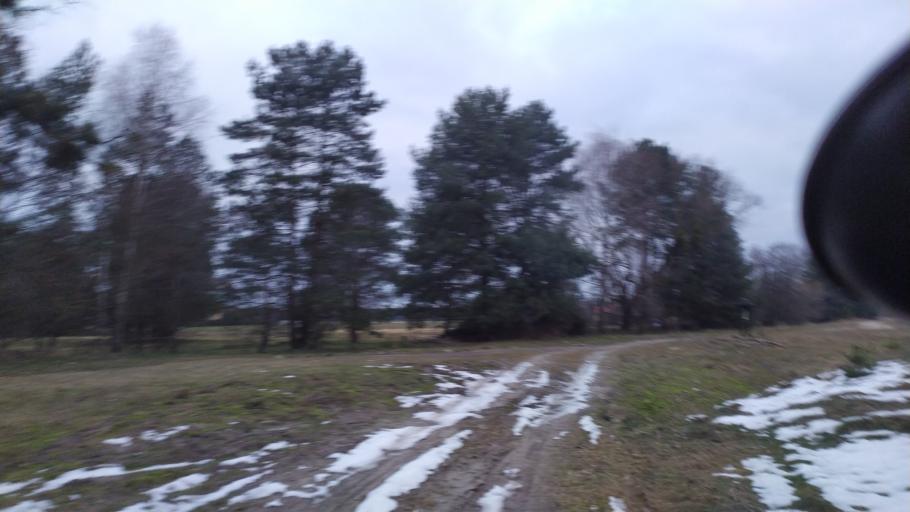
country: PL
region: Lublin Voivodeship
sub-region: Powiat lubartowski
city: Abramow
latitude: 51.4242
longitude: 22.2882
